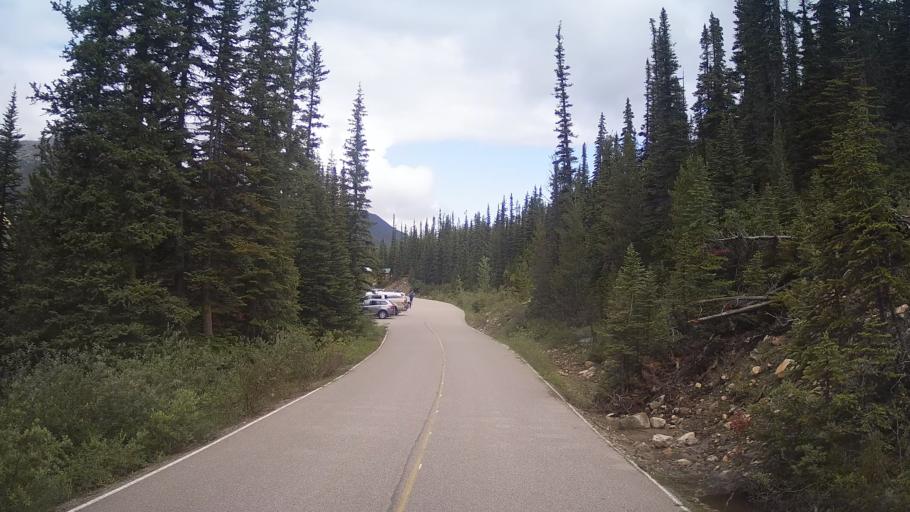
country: CA
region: Alberta
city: Jasper Park Lodge
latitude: 52.7011
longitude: -118.0597
